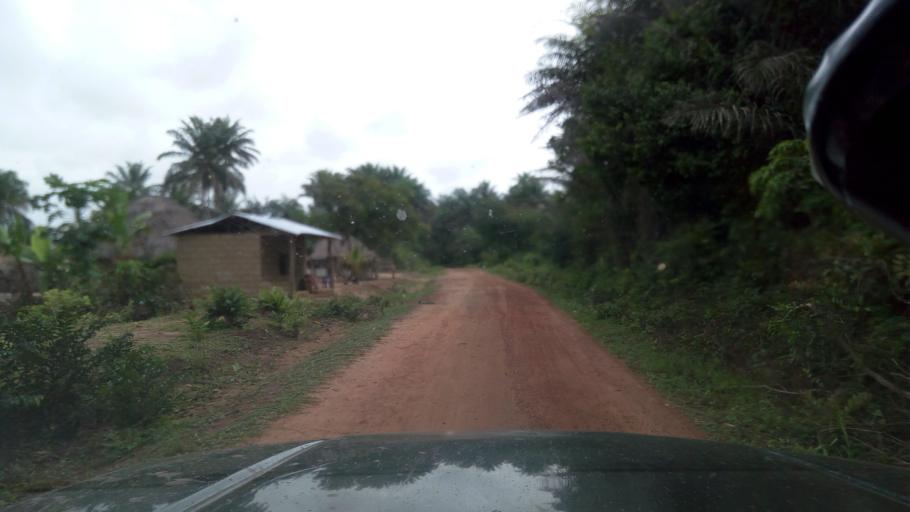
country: SL
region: Northern Province
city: Mange
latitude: 8.8046
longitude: -12.9267
